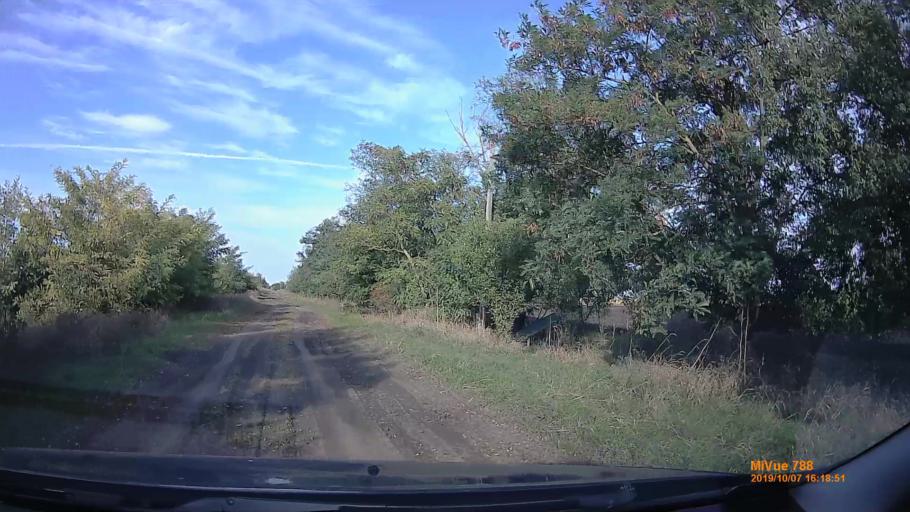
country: HU
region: Bekes
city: Szarvas
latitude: 46.8085
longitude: 20.6255
